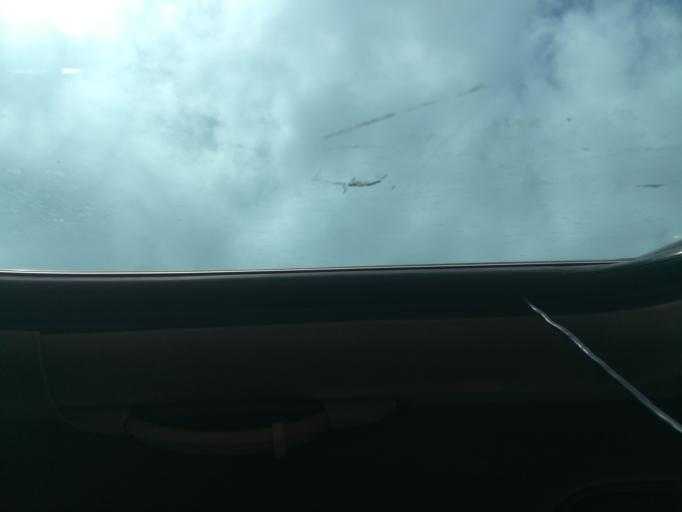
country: NG
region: Lagos
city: Lagos
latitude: 6.4092
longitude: 3.4118
